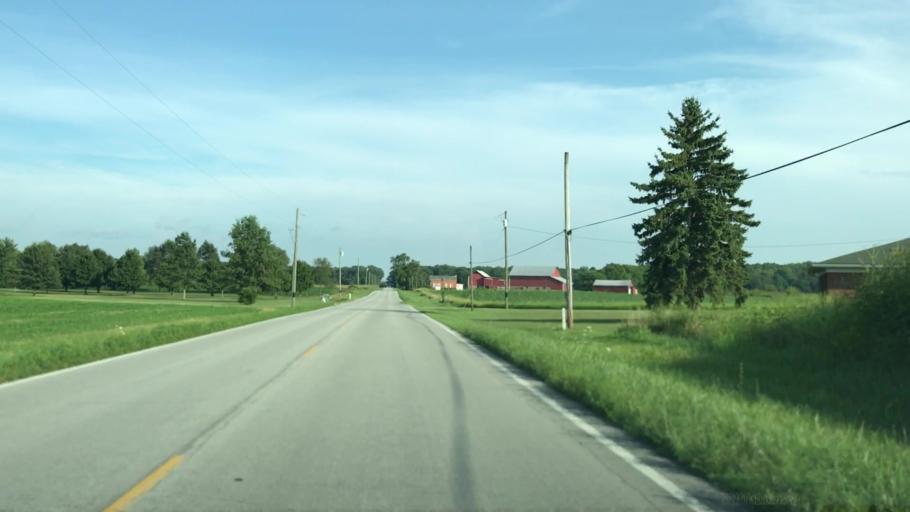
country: US
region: Ohio
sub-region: Union County
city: Marysville
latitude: 40.2001
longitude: -83.3443
